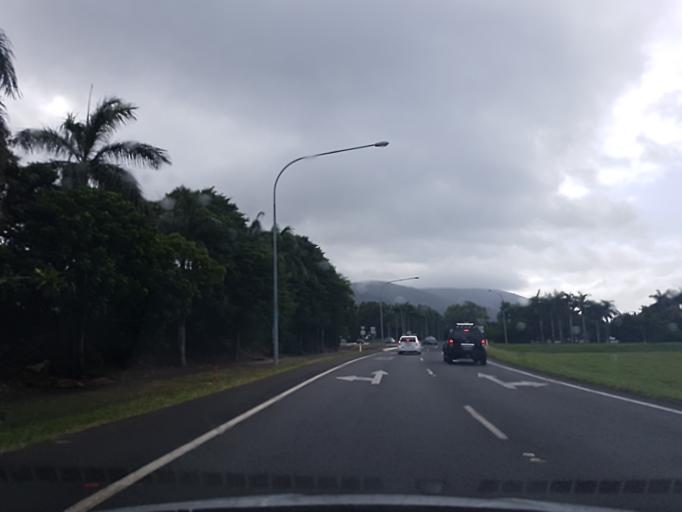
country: AU
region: Queensland
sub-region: Cairns
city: Trinity Beach
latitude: -16.7940
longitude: 145.6793
